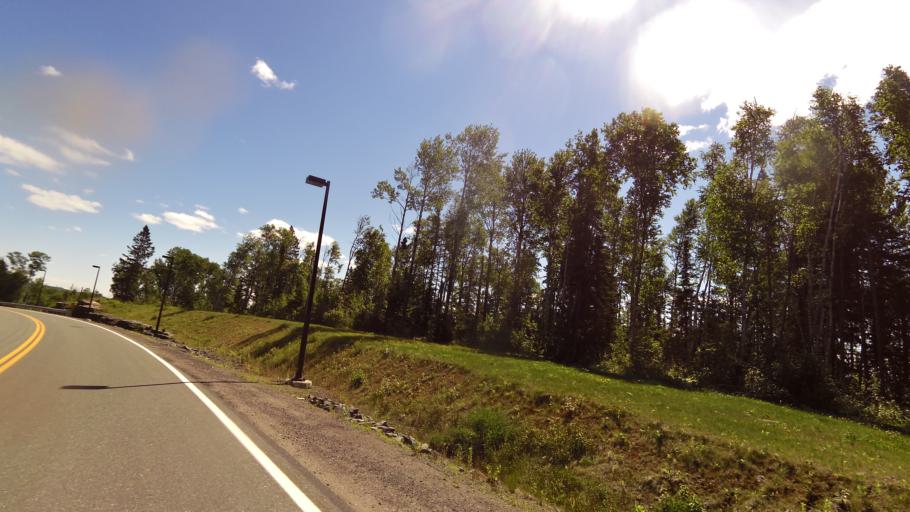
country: CA
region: Ontario
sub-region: Thunder Bay District
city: Thunder Bay
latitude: 48.4863
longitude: -89.1645
